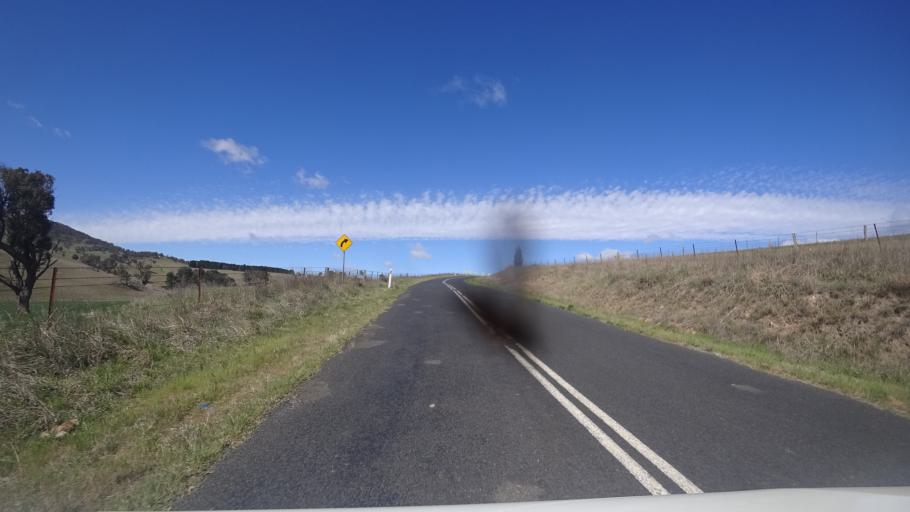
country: AU
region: New South Wales
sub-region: Lithgow
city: Portland
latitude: -33.5182
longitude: 149.9523
